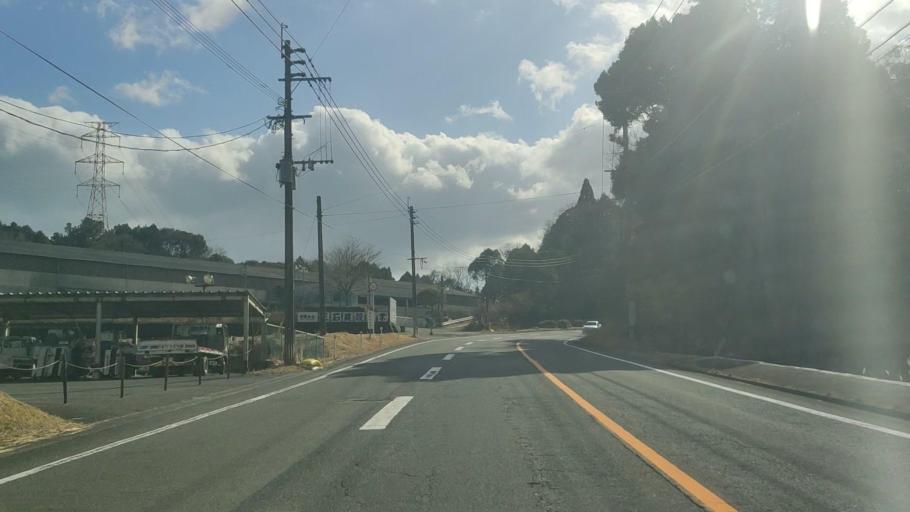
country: JP
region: Kagoshima
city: Okuchi-shinohara
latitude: 31.9301
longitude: 130.7036
